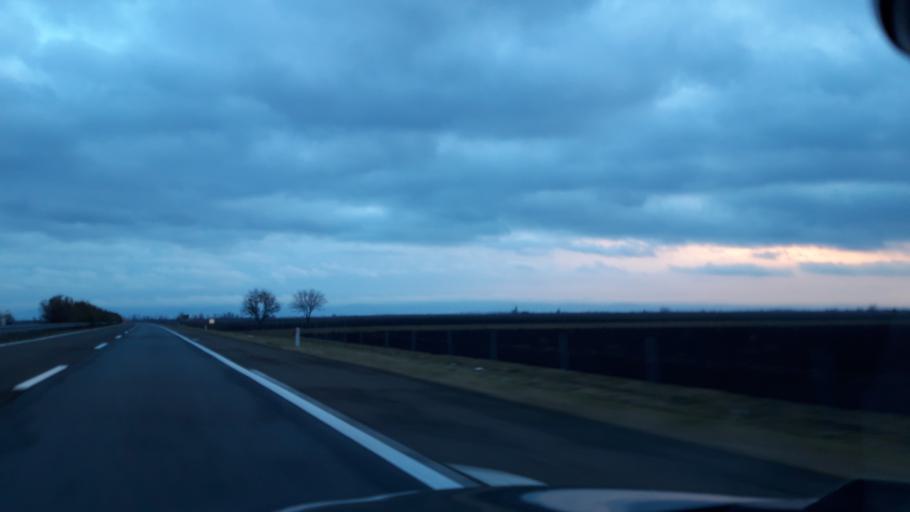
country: RS
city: Kisac
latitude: 45.3600
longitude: 19.7539
